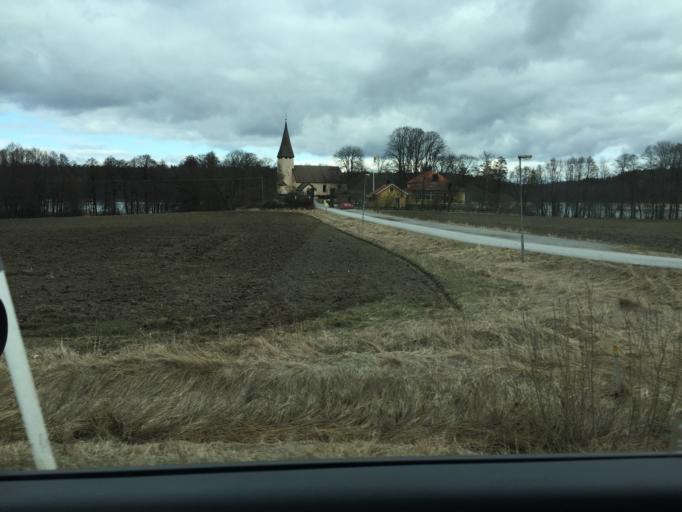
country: SE
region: Stockholm
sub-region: Salems Kommun
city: Ronninge
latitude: 59.2164
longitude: 17.7686
